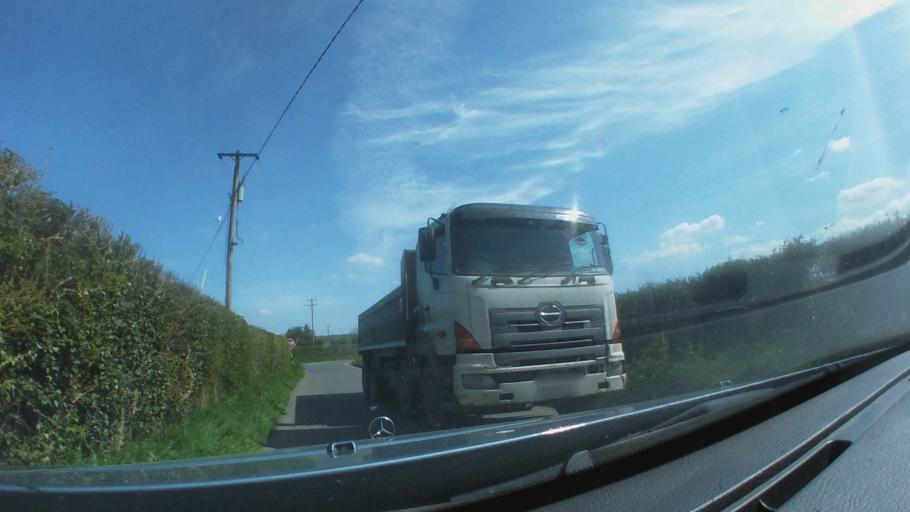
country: IE
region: Leinster
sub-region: Kilkenny
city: Callan
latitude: 52.6240
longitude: -7.4335
